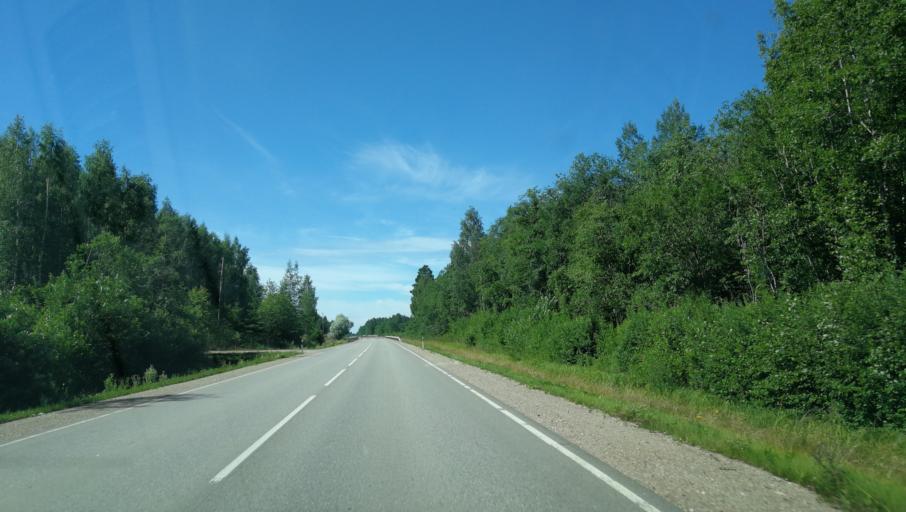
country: LV
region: Gulbenes Rajons
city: Gulbene
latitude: 57.1038
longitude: 26.6483
